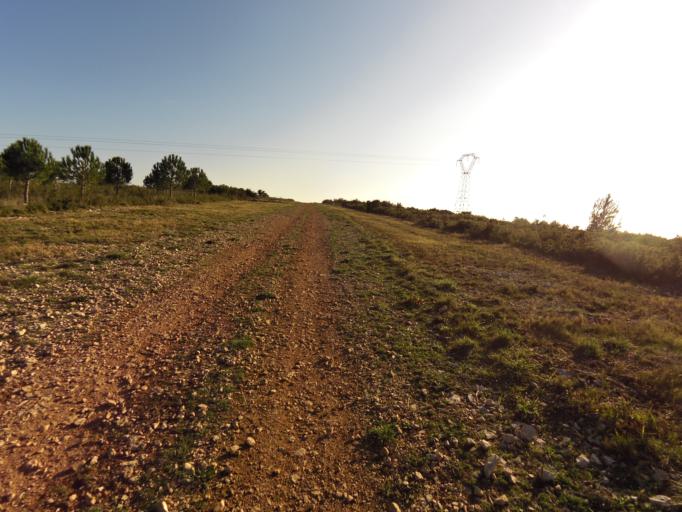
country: FR
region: Languedoc-Roussillon
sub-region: Departement de l'Herault
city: Villetelle
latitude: 43.7336
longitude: 4.1274
